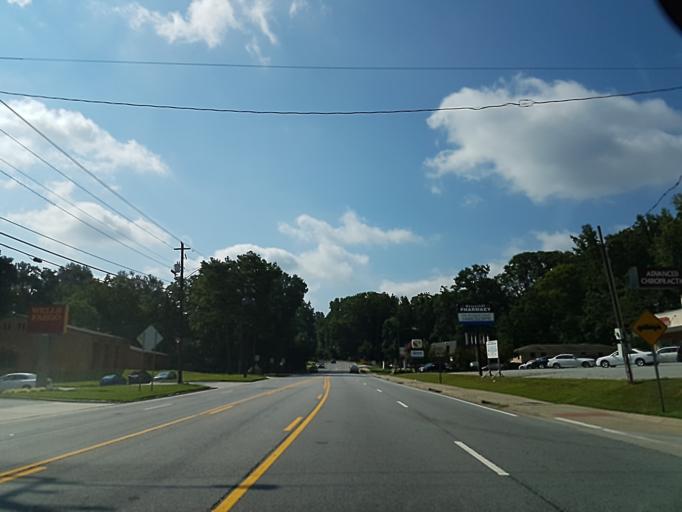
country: US
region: Georgia
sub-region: DeKalb County
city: North Druid Hills
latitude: 33.8367
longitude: -84.3117
